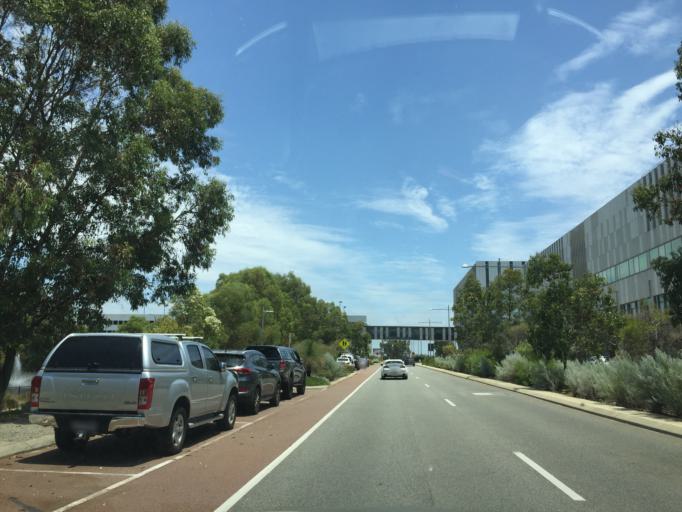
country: AU
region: Western Australia
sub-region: Melville
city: Winthrop
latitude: -32.0713
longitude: 115.8465
